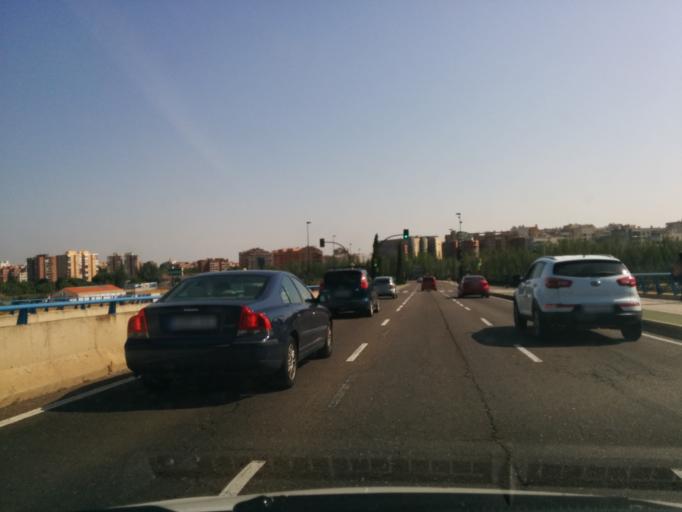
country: ES
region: Aragon
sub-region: Provincia de Zaragoza
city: Zaragoza
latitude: 41.6538
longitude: -0.8616
